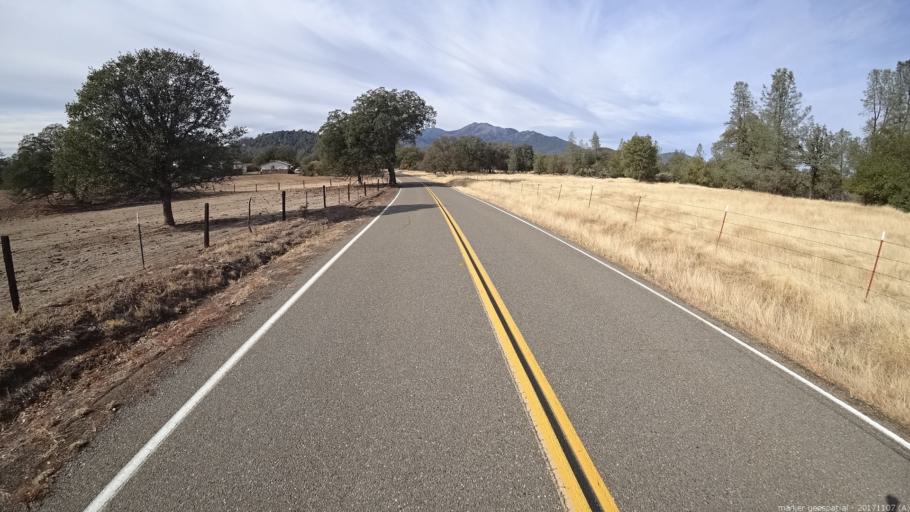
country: US
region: California
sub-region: Shasta County
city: Shasta
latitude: 40.5057
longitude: -122.5347
